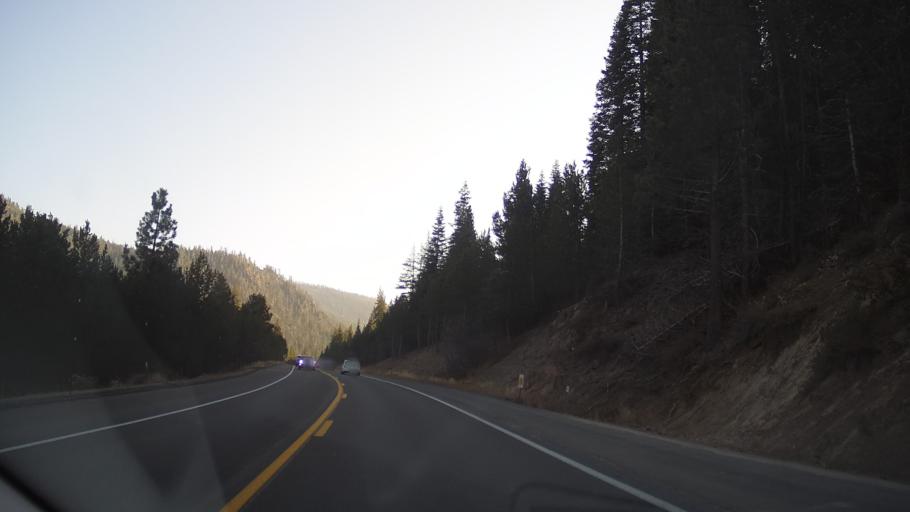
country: US
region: California
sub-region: Placer County
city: Sunnyside-Tahoe City
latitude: 39.2274
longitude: -120.2053
